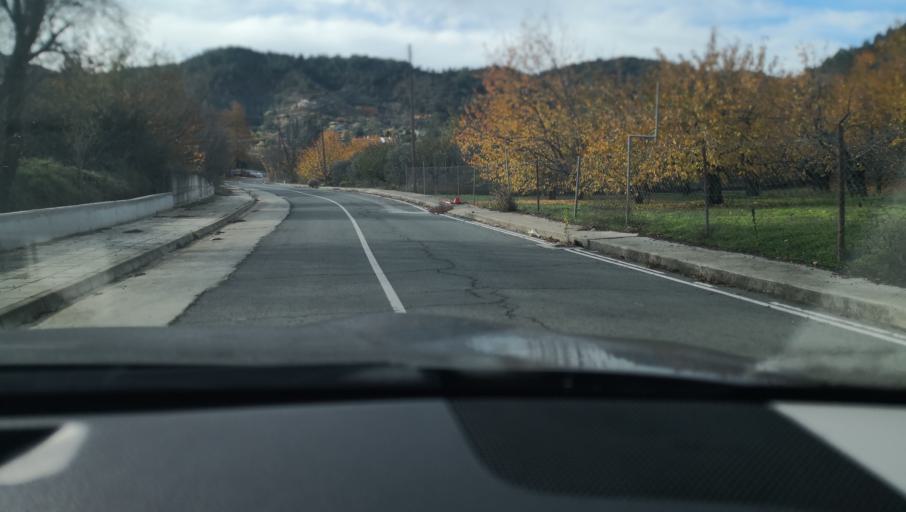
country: CY
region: Lefkosia
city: Lefka
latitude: 35.0287
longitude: 32.7283
